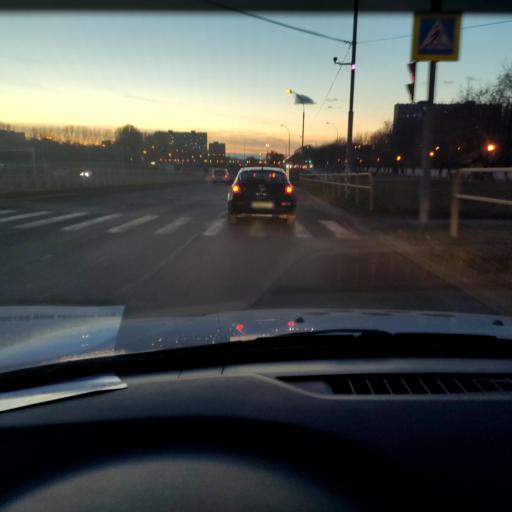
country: RU
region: Samara
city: Tol'yatti
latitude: 53.5203
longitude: 49.2791
